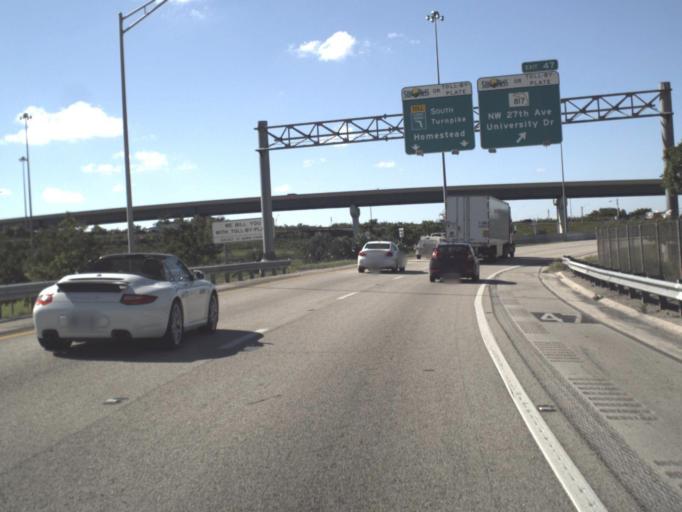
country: US
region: Florida
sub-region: Broward County
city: Miramar
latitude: 25.9751
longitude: -80.2304
